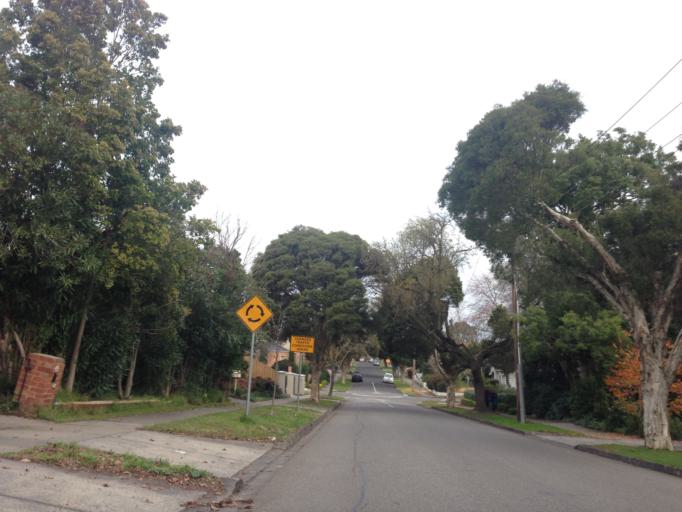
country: AU
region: Victoria
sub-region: Boroondara
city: Kew East
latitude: -37.7976
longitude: 145.0669
